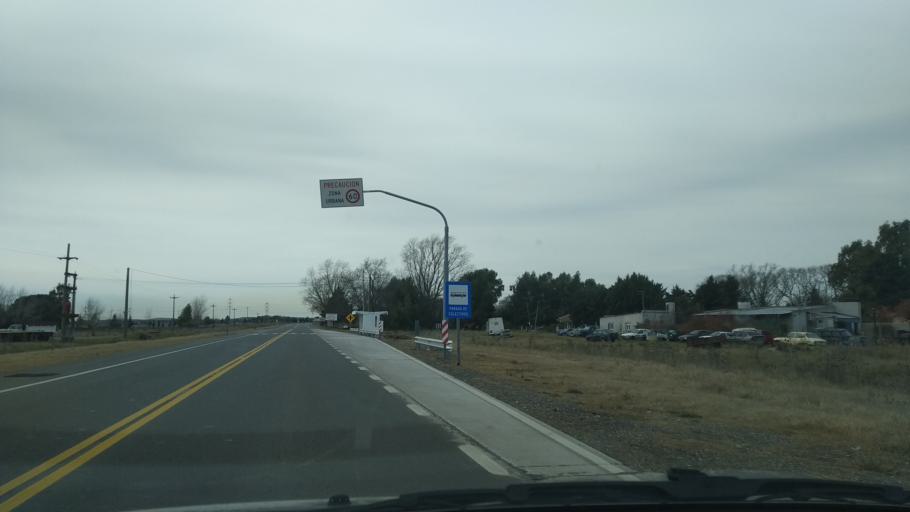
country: AR
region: Buenos Aires
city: Olavarria
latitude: -36.9900
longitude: -60.3123
